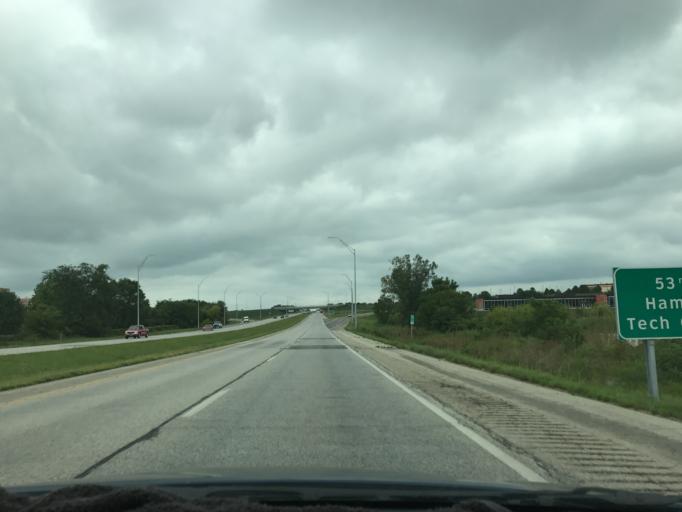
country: US
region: Iowa
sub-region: Scott County
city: Bettendorf
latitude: 41.5682
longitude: -90.5222
